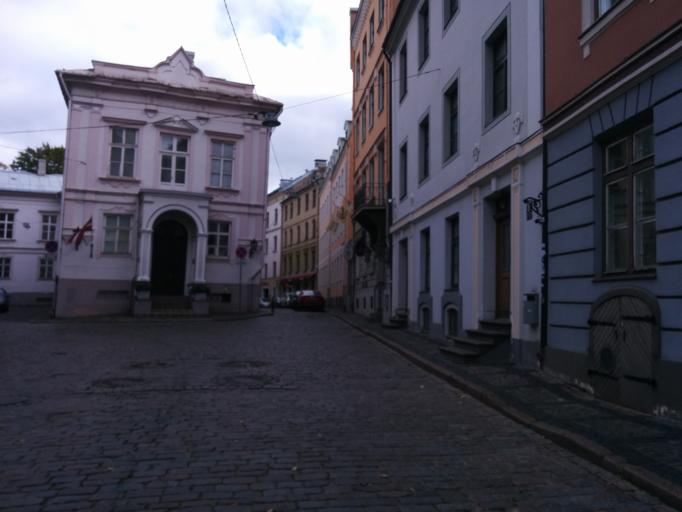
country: LV
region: Riga
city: Riga
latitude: 56.9507
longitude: 24.1023
